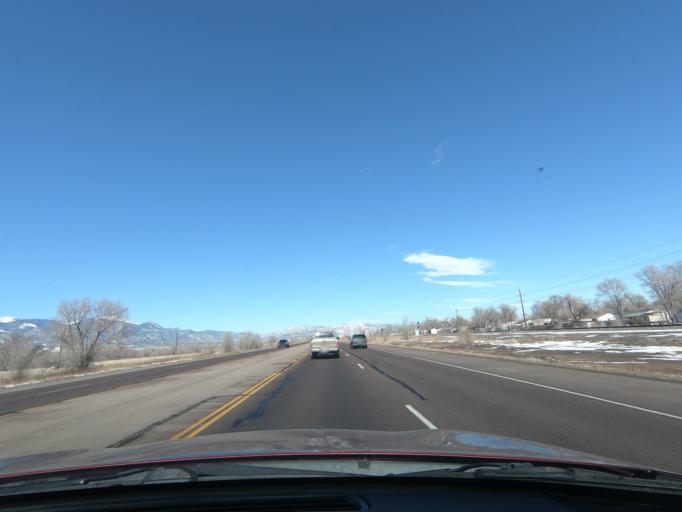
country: US
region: Colorado
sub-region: El Paso County
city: Stratmoor
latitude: 38.7617
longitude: -104.7539
